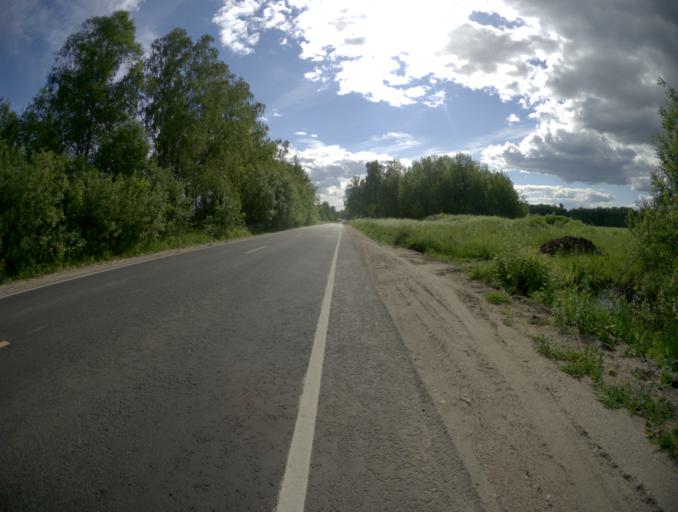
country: RU
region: Ivanovo
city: Kitovo
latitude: 56.8261
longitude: 41.2880
